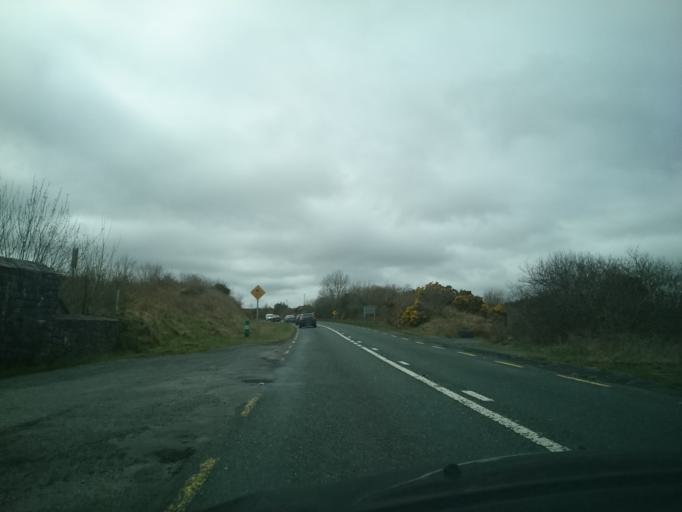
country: IE
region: Connaught
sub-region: Maigh Eo
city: Westport
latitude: 53.8121
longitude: -9.4165
